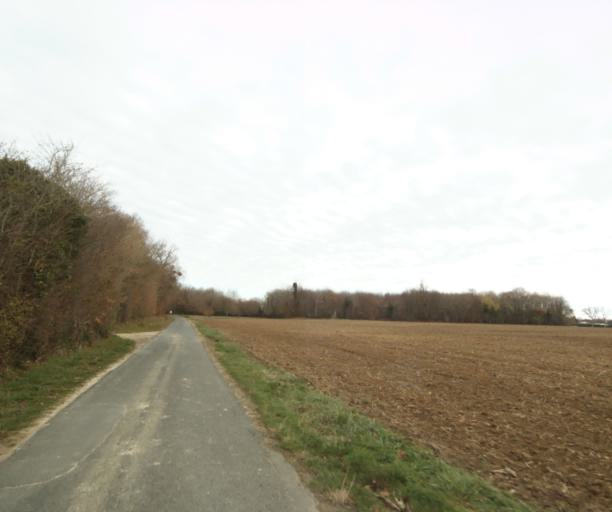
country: FR
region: Poitou-Charentes
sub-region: Departement de la Charente-Maritime
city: Corme-Royal
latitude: 45.7402
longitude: -0.7911
